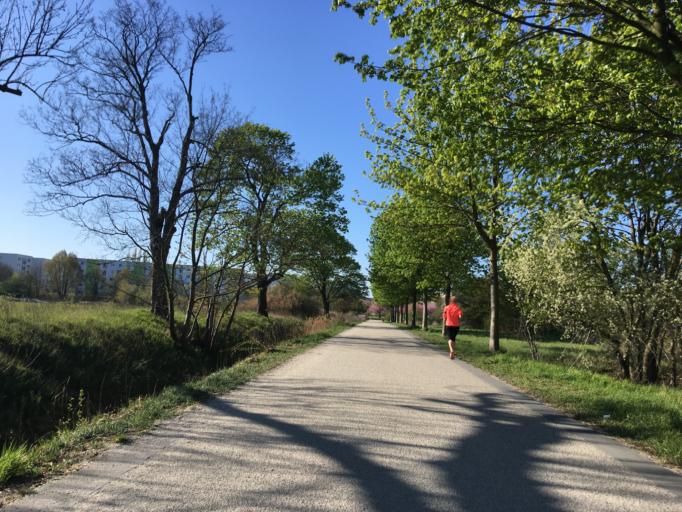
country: DE
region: Berlin
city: Wartenberg
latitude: 52.5797
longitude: 13.5036
